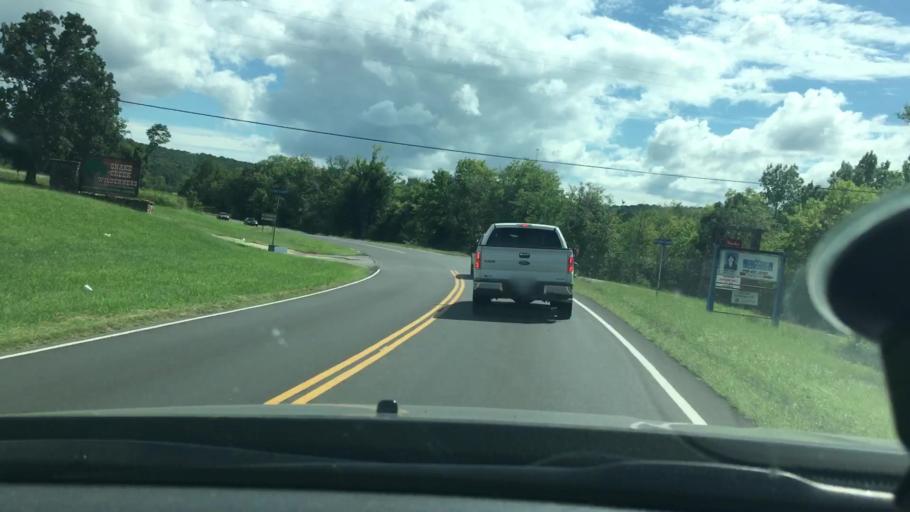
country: US
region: Oklahoma
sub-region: Sequoyah County
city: Vian
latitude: 35.6445
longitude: -94.9612
